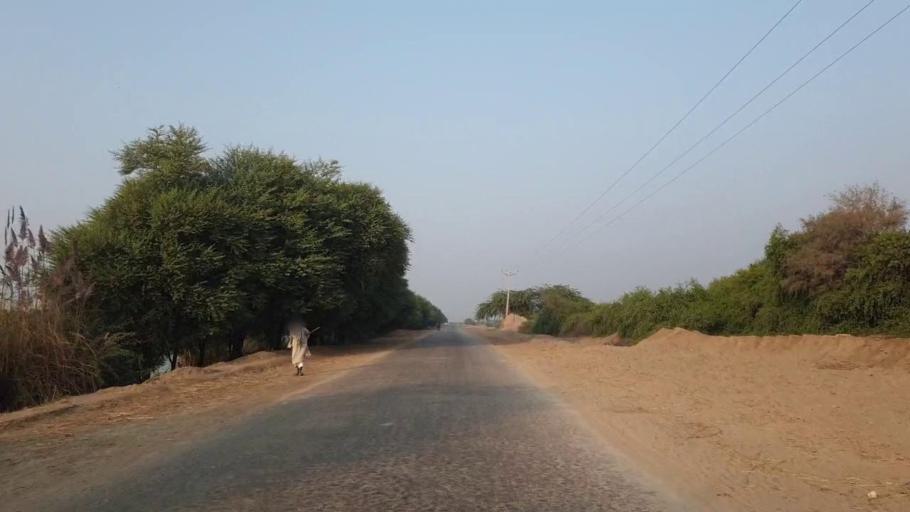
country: PK
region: Sindh
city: Tando Muhammad Khan
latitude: 25.1273
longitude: 68.4321
